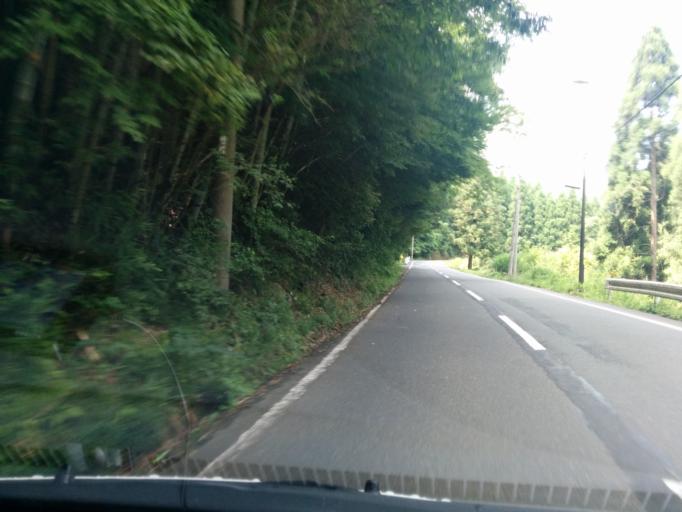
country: JP
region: Kyoto
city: Miyazu
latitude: 35.4356
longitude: 135.1597
